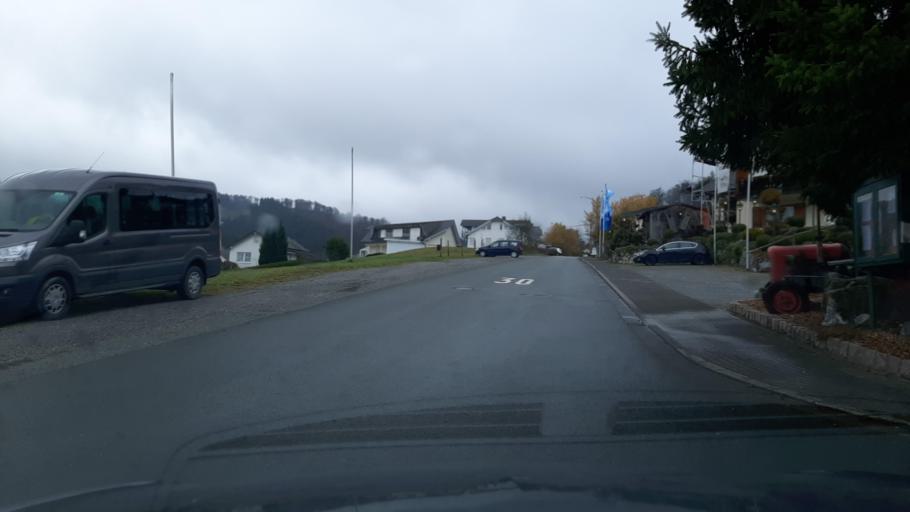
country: DE
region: Hesse
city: Willingen
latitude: 51.2921
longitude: 8.5909
